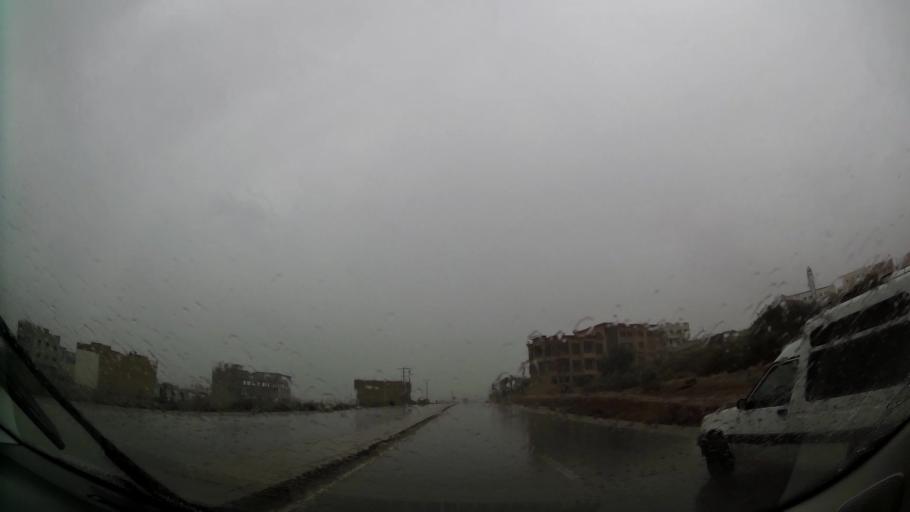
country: MA
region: Taza-Al Hoceima-Taounate
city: Imzourene
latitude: 35.1337
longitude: -3.8464
